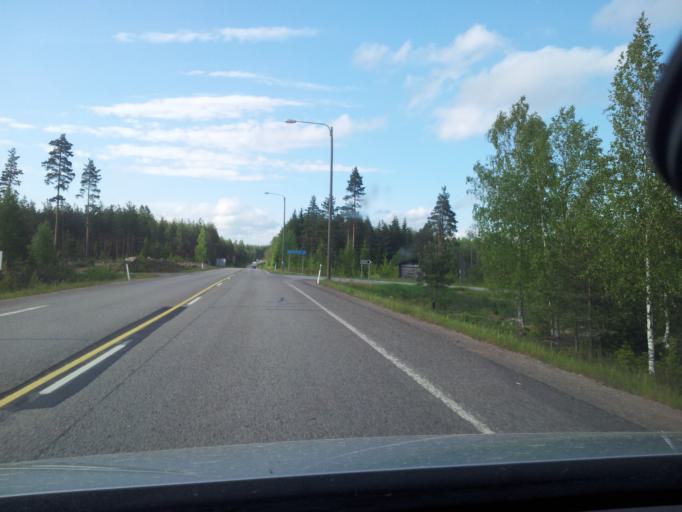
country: FI
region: South Karelia
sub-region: Lappeenranta
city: Luumaeki
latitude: 60.9303
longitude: 27.5839
